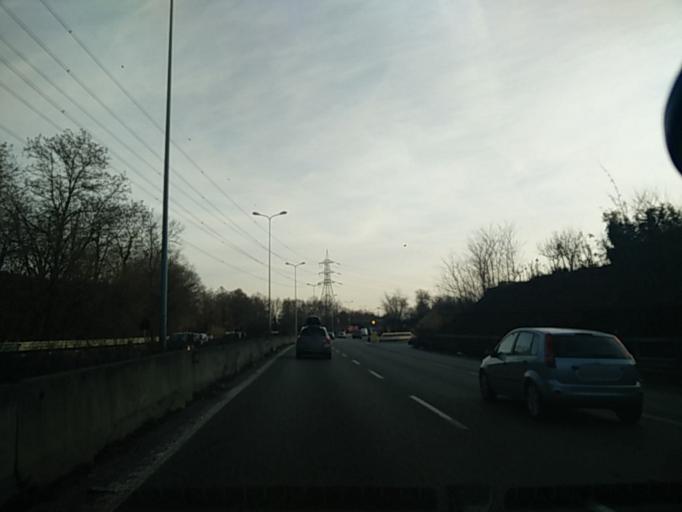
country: IT
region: Lombardy
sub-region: Provincia di Monza e Brianza
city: Varedo
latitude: 45.5994
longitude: 9.1711
